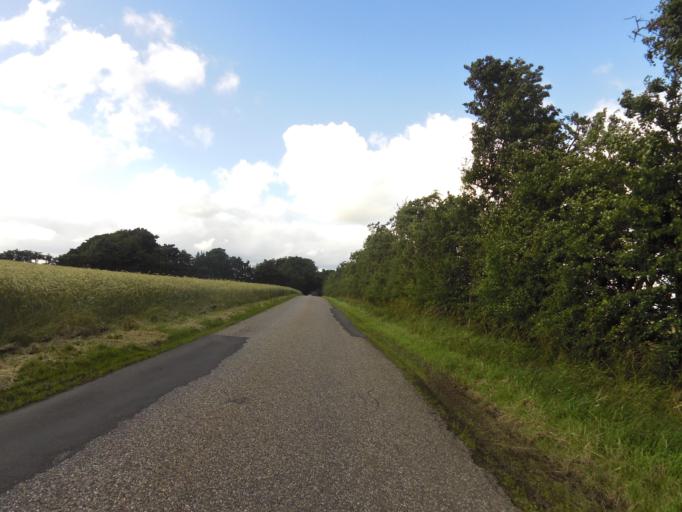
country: DK
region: South Denmark
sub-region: Tonder Kommune
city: Toftlund
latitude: 55.1452
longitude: 9.0845
